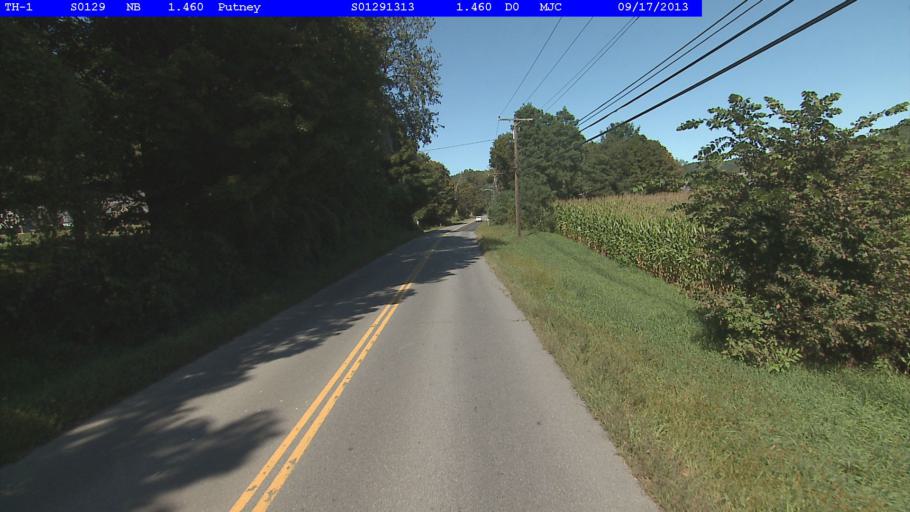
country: US
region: New Hampshire
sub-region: Cheshire County
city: Westmoreland
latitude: 42.9936
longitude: -72.5318
